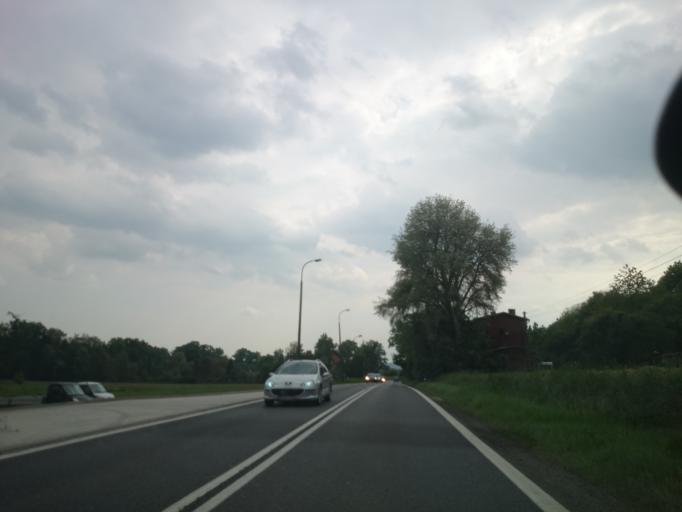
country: PL
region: Lower Silesian Voivodeship
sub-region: Powiat dzierzoniowski
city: Niemcza
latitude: 50.7469
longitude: 16.8428
